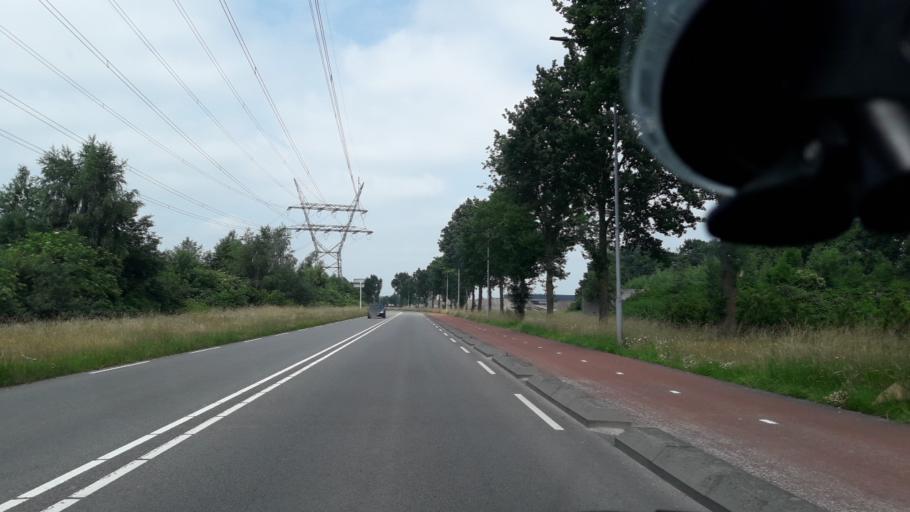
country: NL
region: Gelderland
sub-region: Gemeente Harderwijk
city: Harderwijk
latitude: 52.3548
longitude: 5.6527
